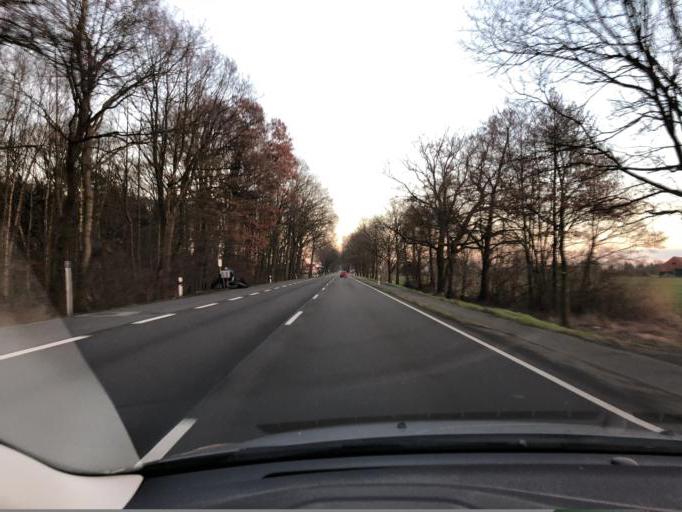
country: DE
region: Lower Saxony
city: Engeln
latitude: 52.8209
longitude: 8.9435
